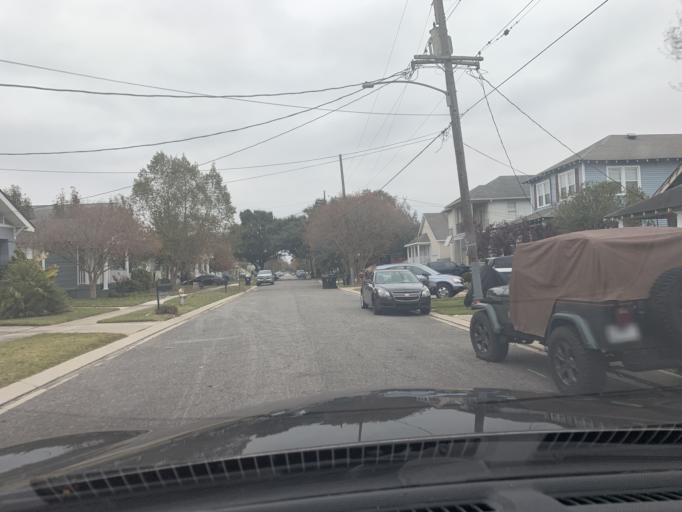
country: US
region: Louisiana
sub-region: Jefferson Parish
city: Metairie
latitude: 29.9966
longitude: -90.1142
